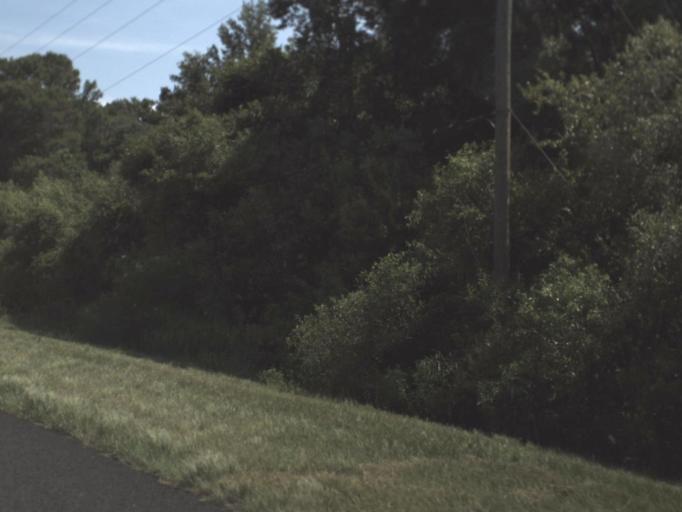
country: US
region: Florida
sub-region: Marion County
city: Citra
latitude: 29.4480
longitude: -82.1086
